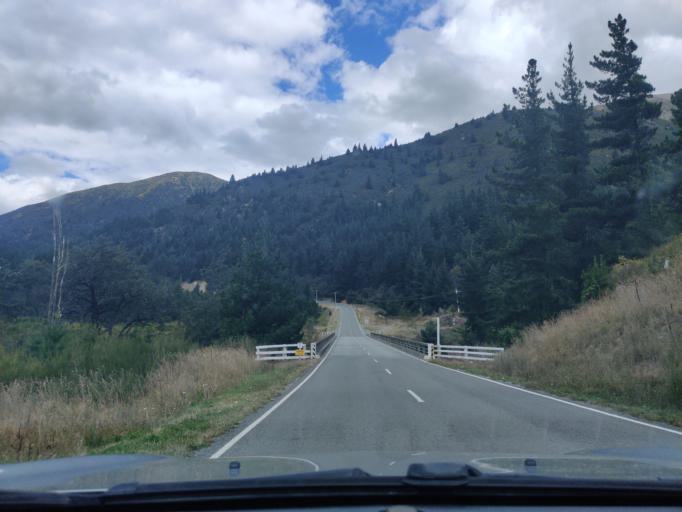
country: NZ
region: Canterbury
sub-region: Hurunui District
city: Amberley
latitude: -42.5829
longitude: 172.6203
